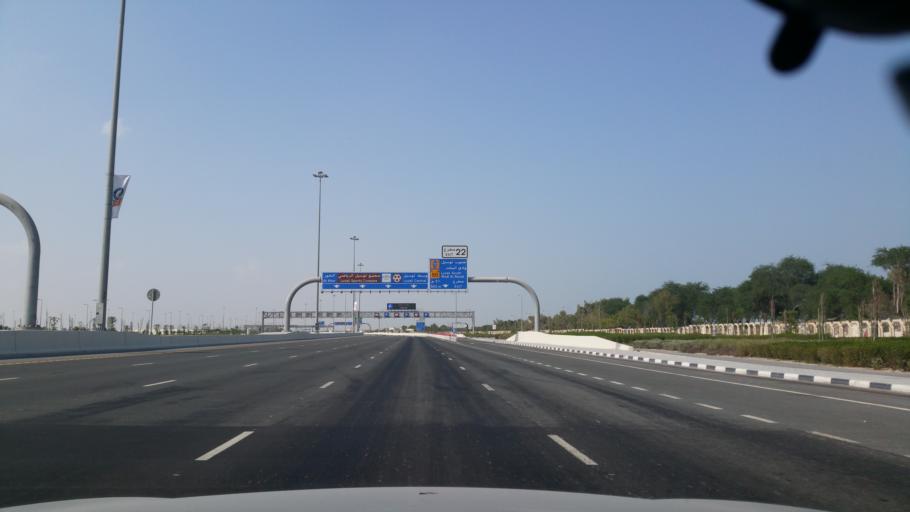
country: QA
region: Baladiyat Umm Salal
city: Umm Salal Muhammad
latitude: 25.3819
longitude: 51.5003
